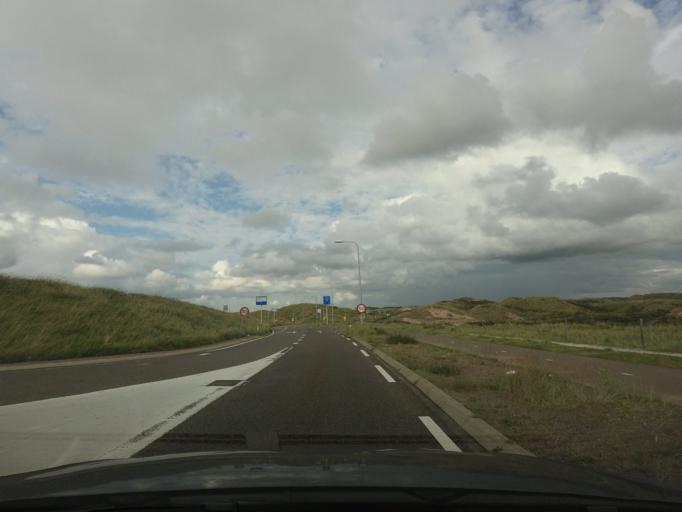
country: NL
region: North Holland
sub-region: Gemeente Zandvoort
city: Zandvoort
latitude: 52.4023
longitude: 4.5466
